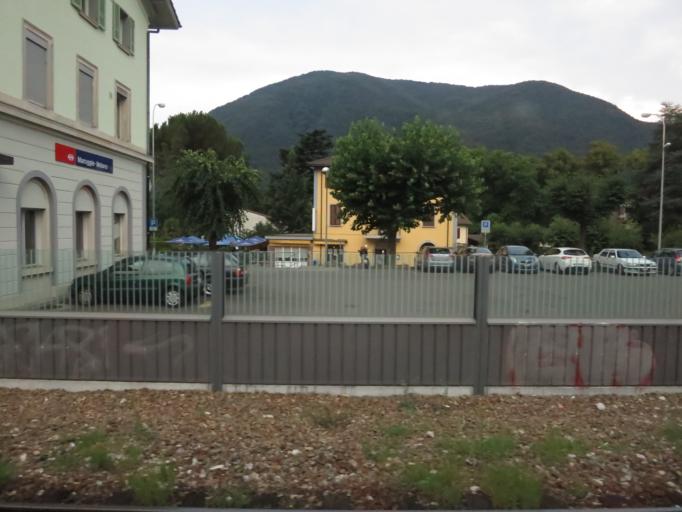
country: CH
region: Ticino
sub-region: Lugano District
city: Melano
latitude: 45.9328
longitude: 8.9737
